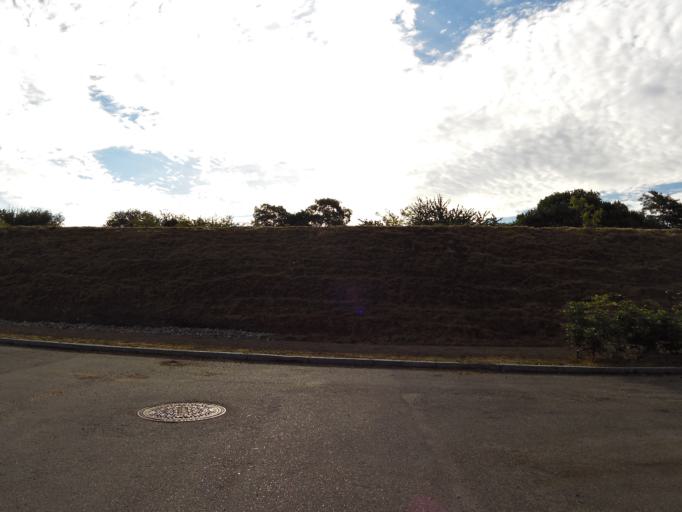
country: DK
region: Capital Region
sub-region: Fredensborg Kommune
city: Niva
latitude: 55.9436
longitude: 12.4881
